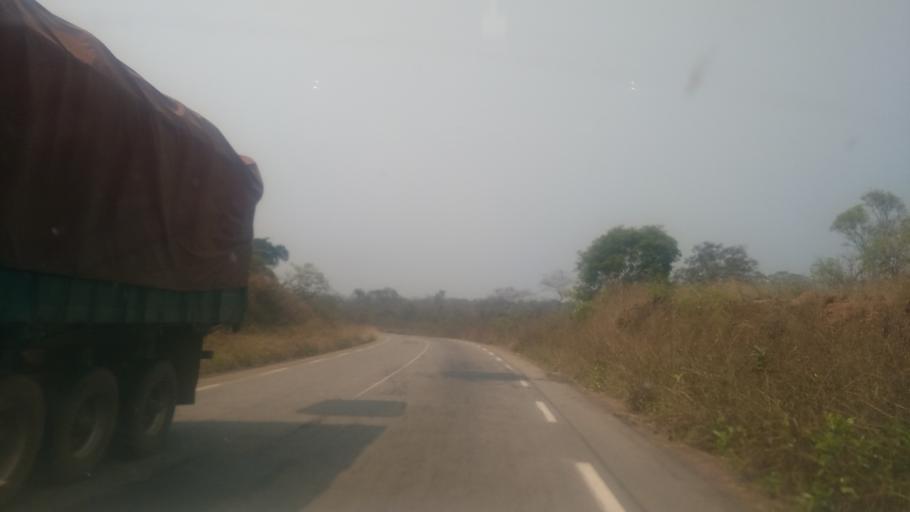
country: CM
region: Centre
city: Bafia
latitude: 4.8504
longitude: 11.0715
